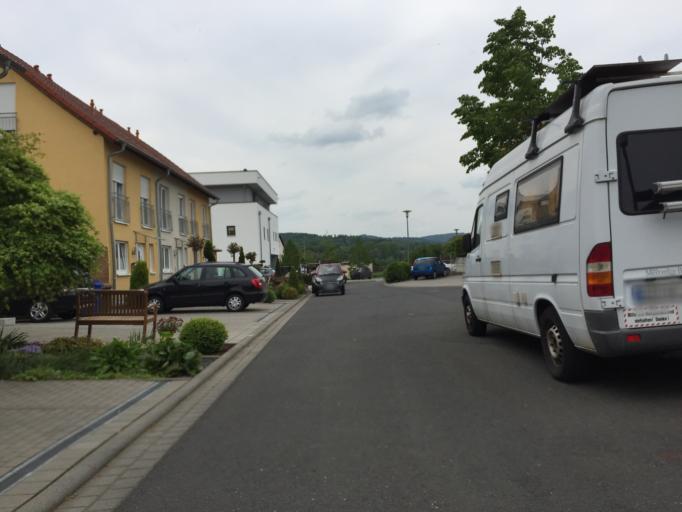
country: DE
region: Bavaria
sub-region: Regierungsbezirk Unterfranken
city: Hosbach
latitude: 50.0103
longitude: 9.2082
